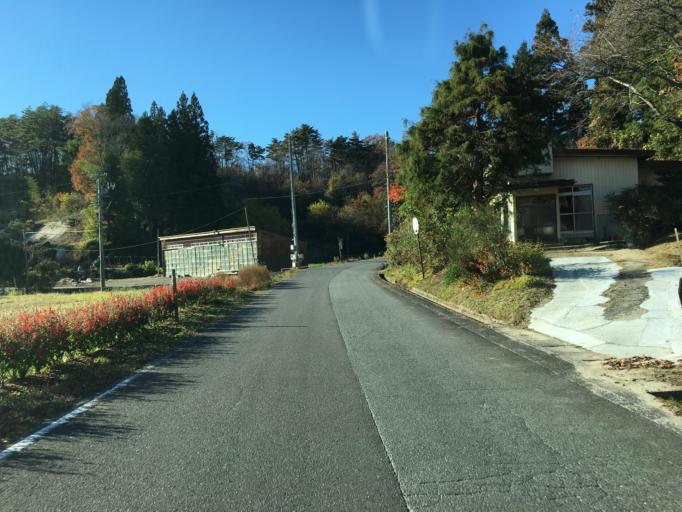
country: JP
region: Fukushima
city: Ishikawa
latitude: 37.2240
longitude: 140.5230
